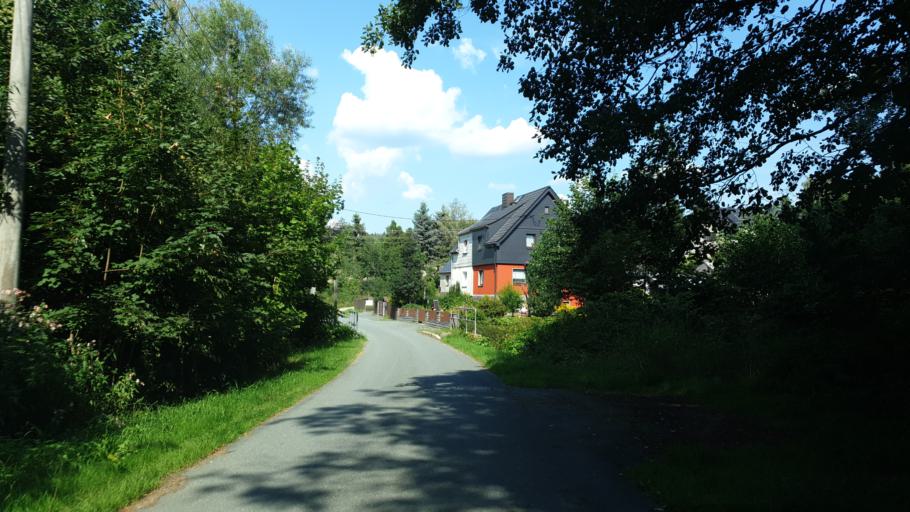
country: DE
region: Saxony
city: Pohl
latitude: 50.4008
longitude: 12.3285
